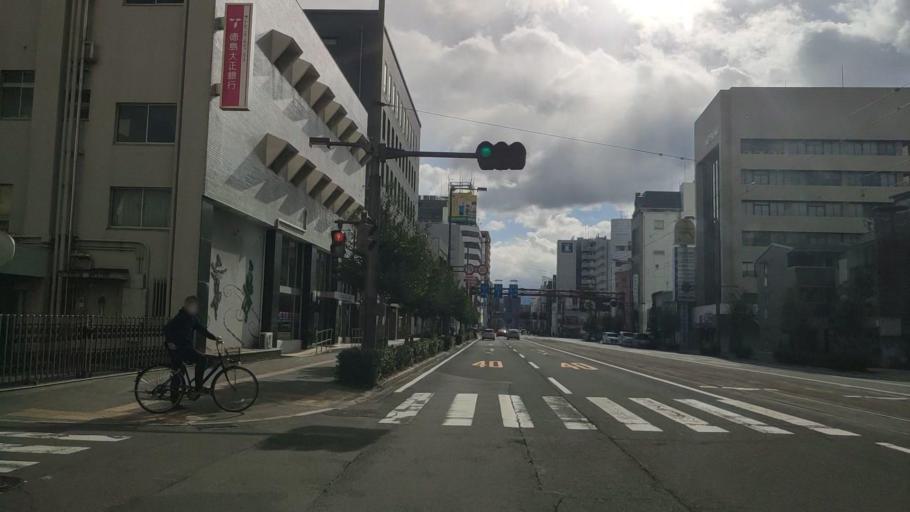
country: JP
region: Ehime
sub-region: Shikoku-chuo Shi
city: Matsuyama
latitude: 33.8434
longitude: 132.7755
